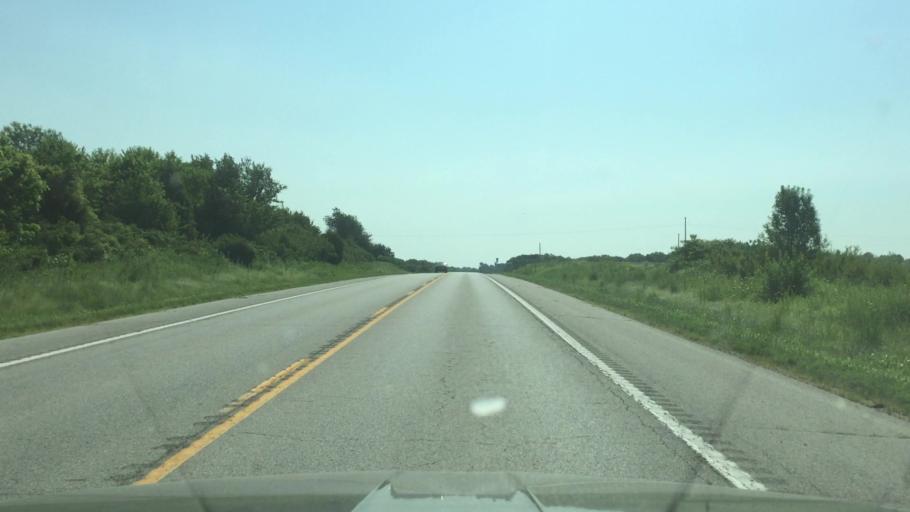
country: US
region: Missouri
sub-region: Pettis County
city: Sedalia
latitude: 38.6938
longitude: -93.1002
